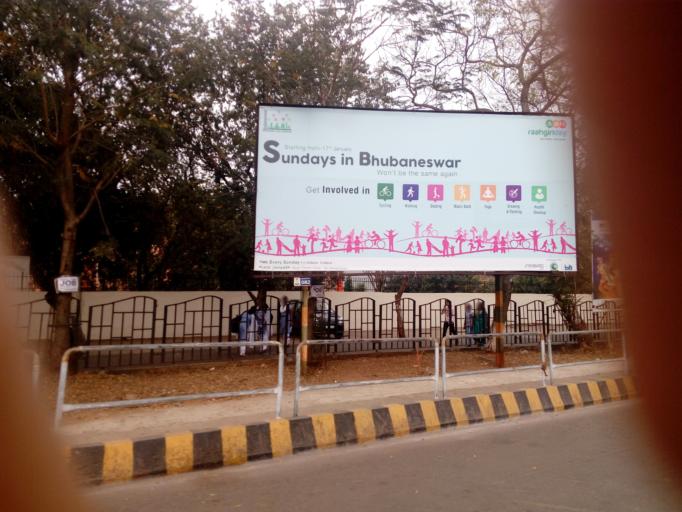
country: IN
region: Odisha
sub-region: Khordha
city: Bhubaneshwar
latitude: 20.2919
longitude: 85.8423
